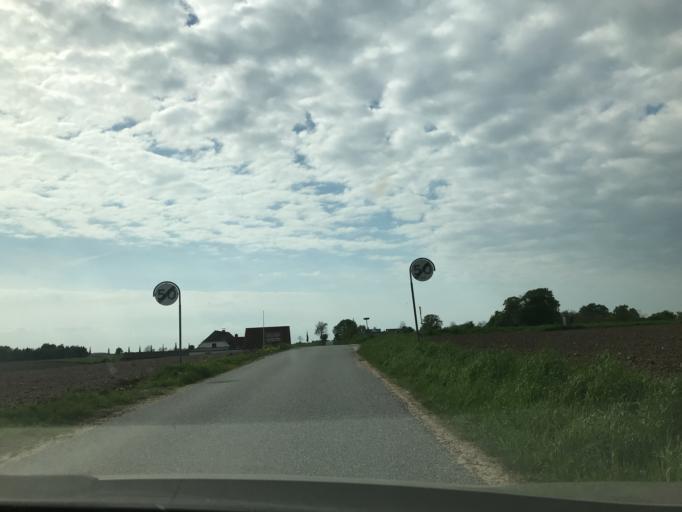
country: DK
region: South Denmark
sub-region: Middelfart Kommune
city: Ejby
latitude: 55.3596
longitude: 9.8724
